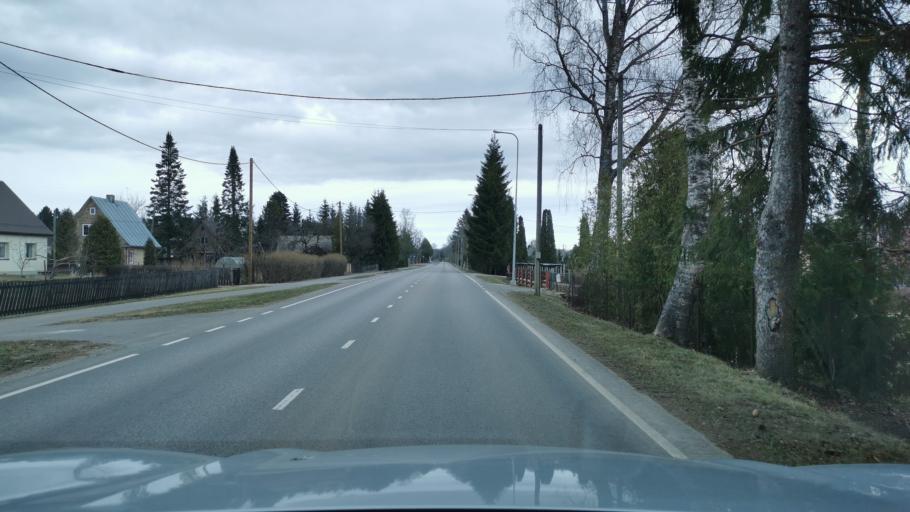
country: EE
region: Ida-Virumaa
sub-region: Kivioli linn
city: Kivioli
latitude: 59.3396
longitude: 27.0117
